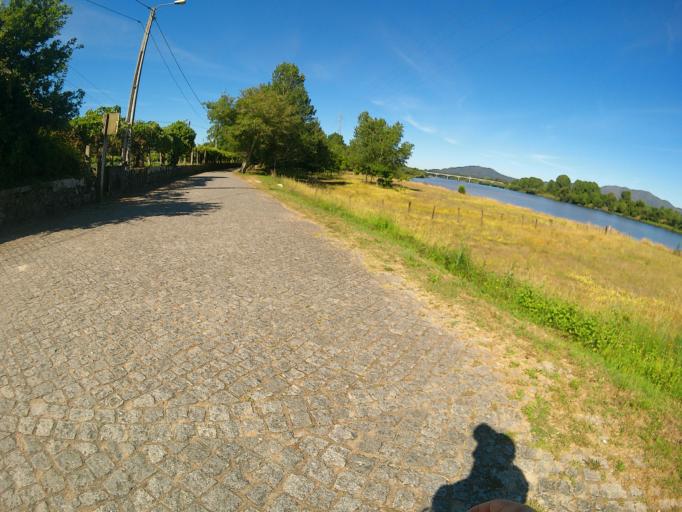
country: PT
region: Viana do Castelo
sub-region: Ponte de Lima
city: Ponte de Lima
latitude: 41.7261
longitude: -8.6717
